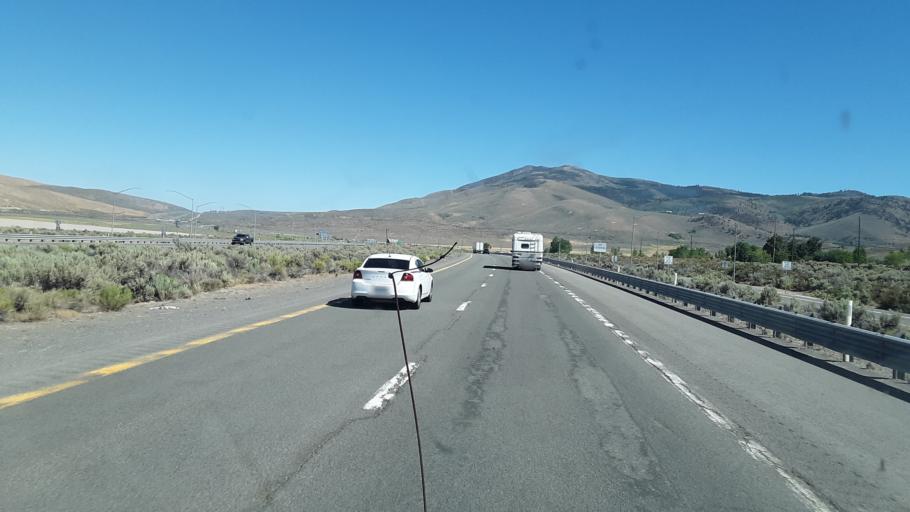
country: US
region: Nevada
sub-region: Washoe County
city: Cold Springs
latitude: 39.6562
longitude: -119.9867
